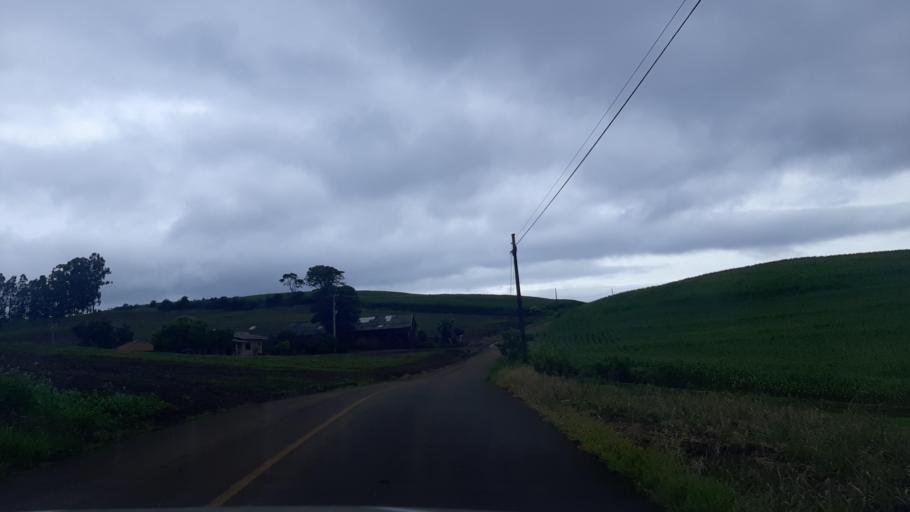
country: BR
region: Parana
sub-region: Ampere
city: Ampere
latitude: -26.0408
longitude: -53.4925
